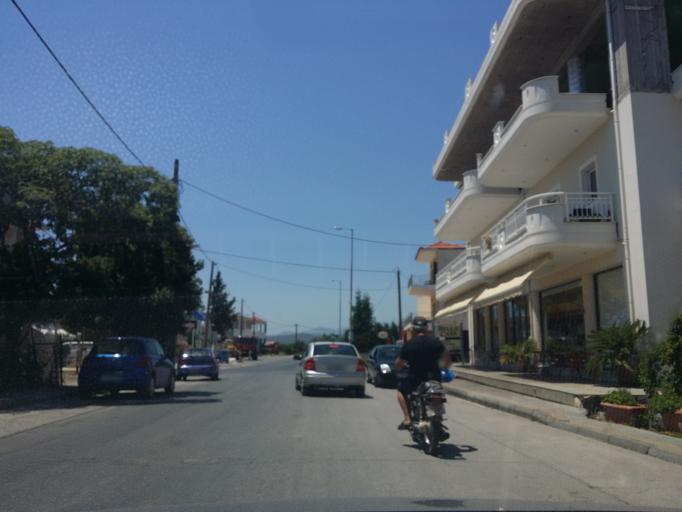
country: GR
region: Peloponnese
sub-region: Nomos Lakonias
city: Skala
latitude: 36.8485
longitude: 22.6603
